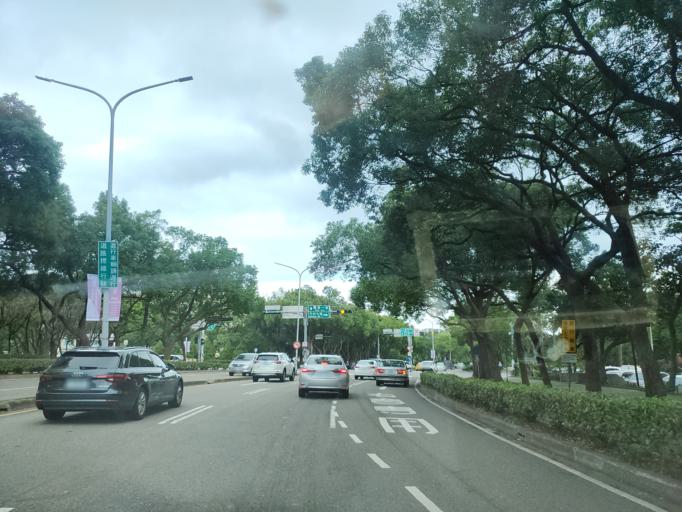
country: TW
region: Taiwan
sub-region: Hsinchu
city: Hsinchu
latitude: 24.7800
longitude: 121.0064
